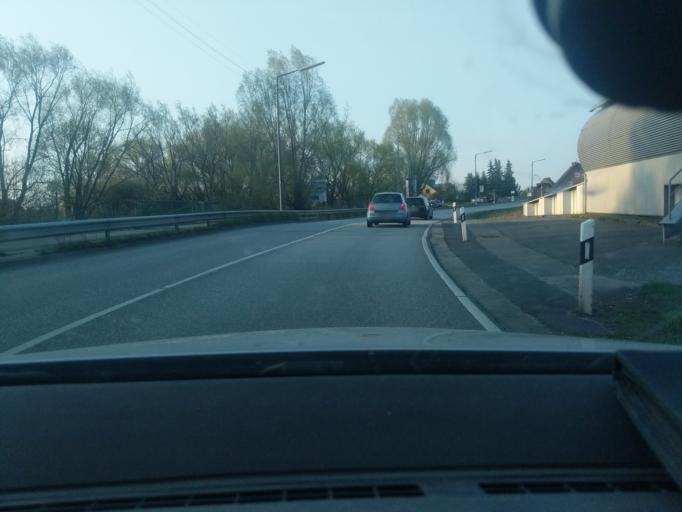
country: DE
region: Hamburg
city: Altona
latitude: 53.5188
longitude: 9.8850
